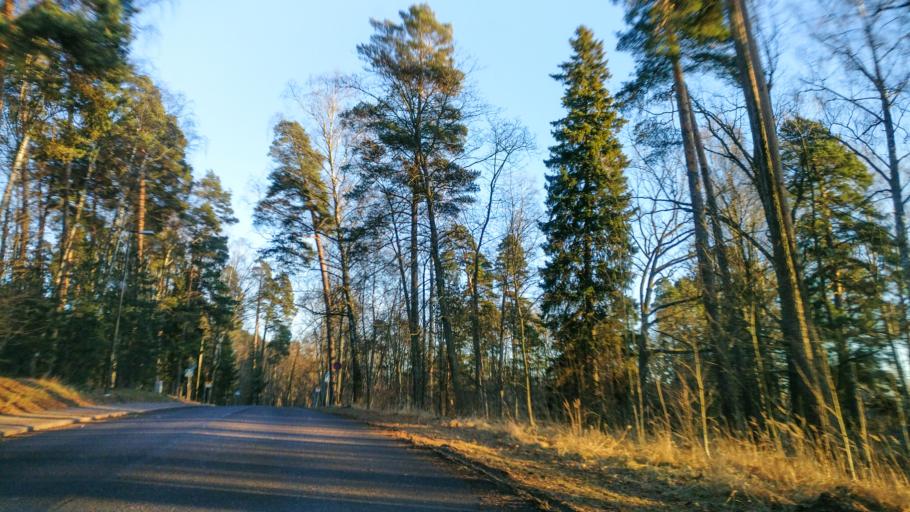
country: FI
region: Uusimaa
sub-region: Helsinki
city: Helsinki
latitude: 60.1874
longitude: 24.8941
